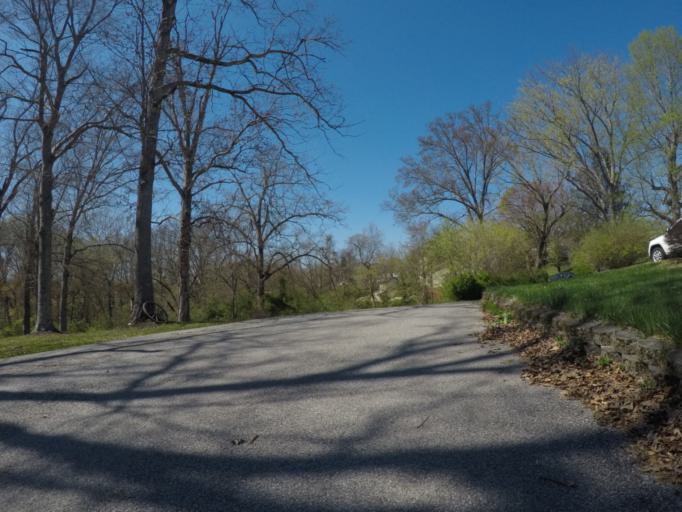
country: US
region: West Virginia
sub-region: Cabell County
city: Pea Ridge
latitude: 38.4147
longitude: -82.3155
